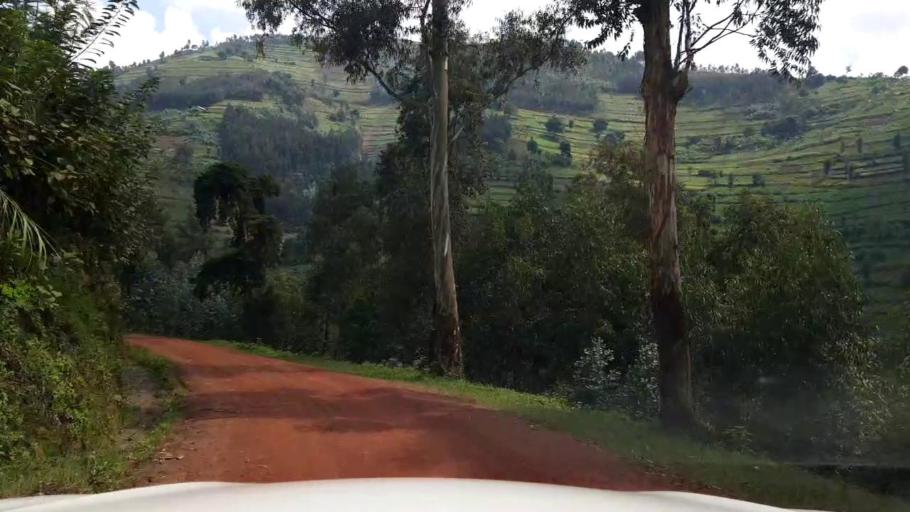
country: UG
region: Western Region
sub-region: Kisoro District
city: Kisoro
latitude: -1.3824
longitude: 29.7943
